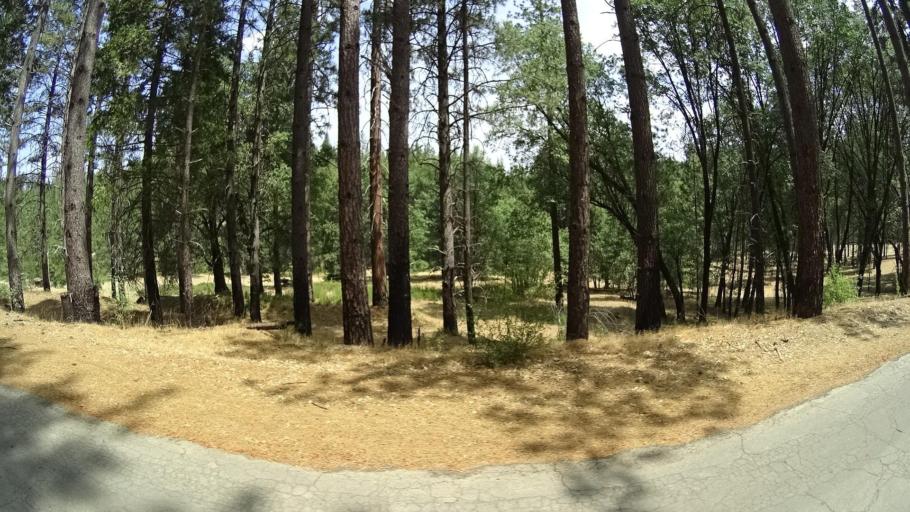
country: US
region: California
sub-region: Mariposa County
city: Midpines
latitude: 37.7507
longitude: -120.0449
